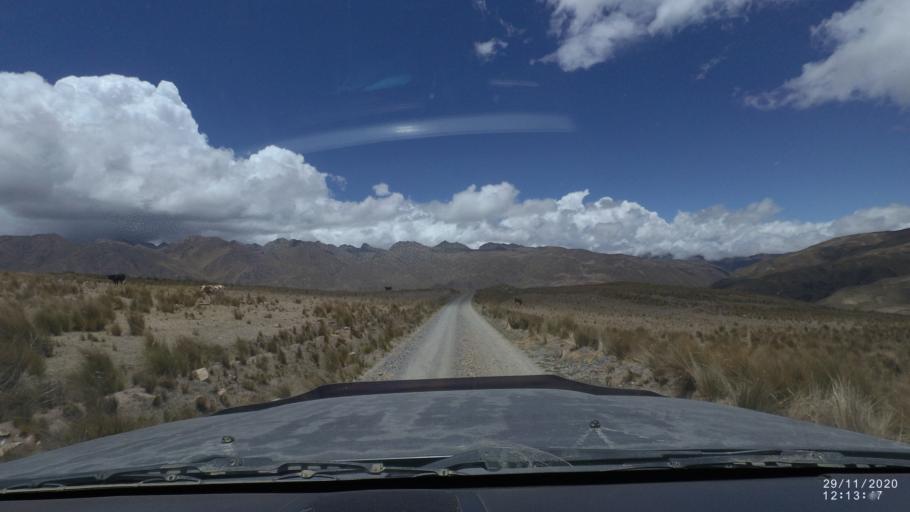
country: BO
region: Cochabamba
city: Cochabamba
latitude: -17.1093
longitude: -66.3095
